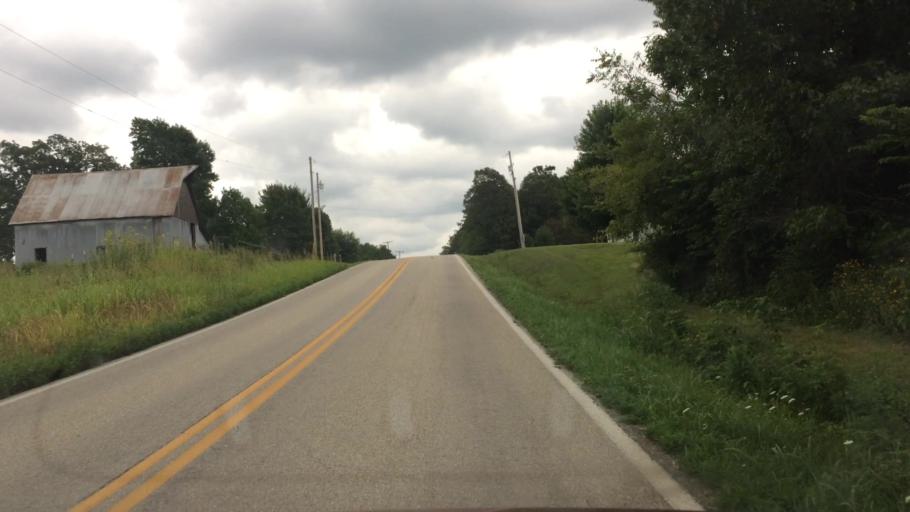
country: US
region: Missouri
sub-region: Greene County
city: Strafford
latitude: 37.3003
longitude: -93.1556
